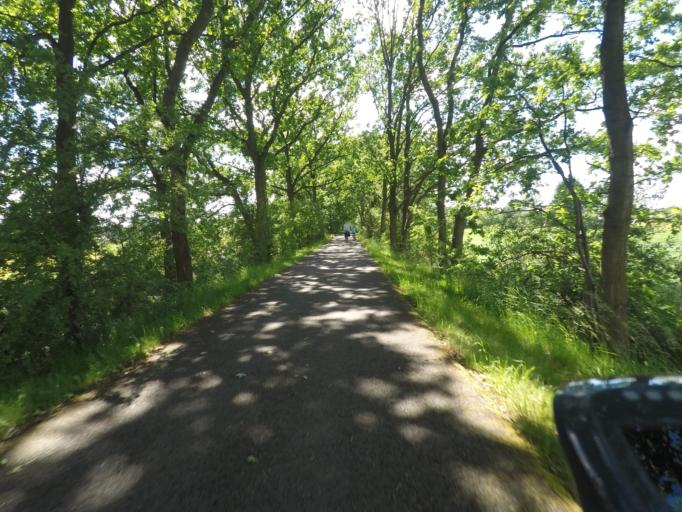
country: DE
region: Hamburg
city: Bergedorf
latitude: 53.4318
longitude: 10.2079
